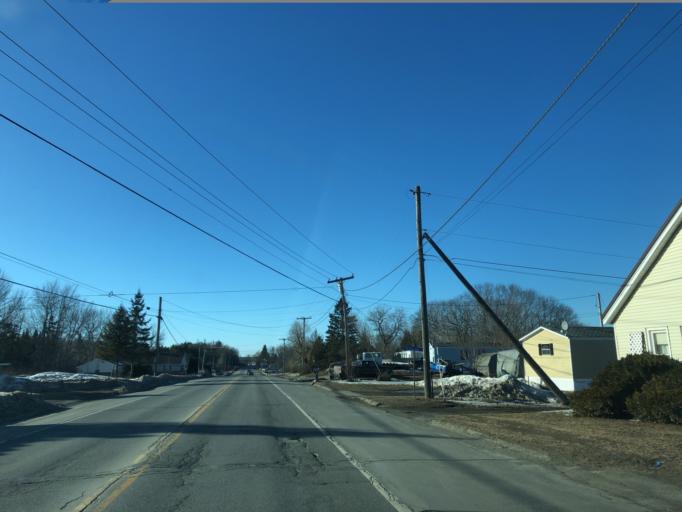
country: US
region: Maine
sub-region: Penobscot County
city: Kenduskeag
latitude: 44.8915
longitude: -68.8764
